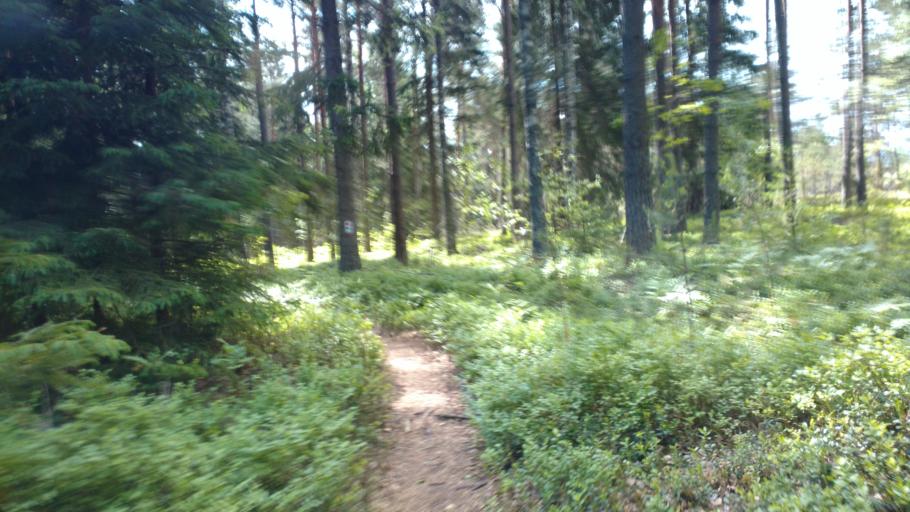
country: FI
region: Uusimaa
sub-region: Raaseporin
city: Pohja
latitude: 60.1092
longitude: 23.5512
